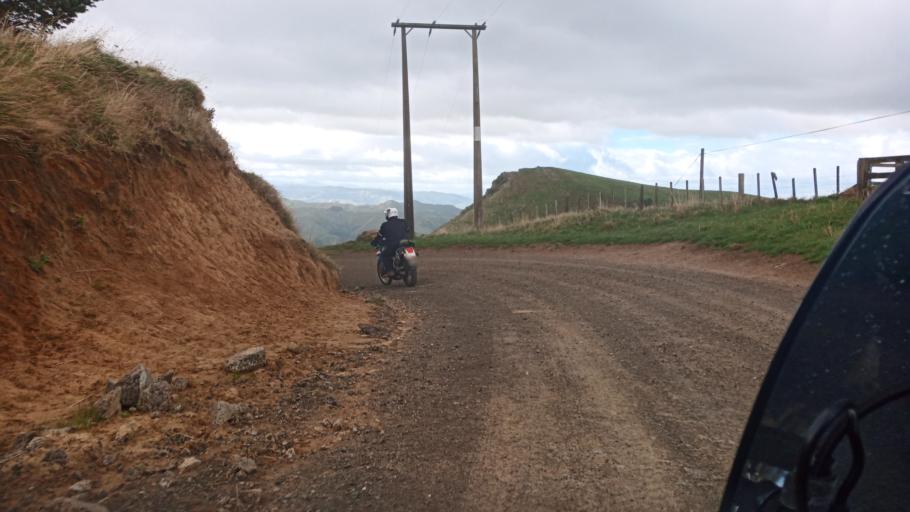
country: NZ
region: Gisborne
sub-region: Gisborne District
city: Gisborne
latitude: -38.4835
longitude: 177.6071
